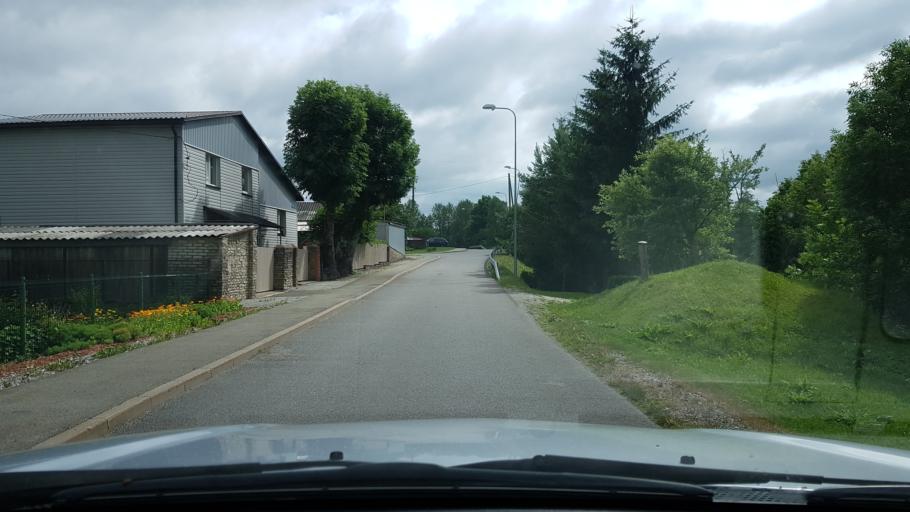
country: EE
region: Ida-Virumaa
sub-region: Narva linn
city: Narva
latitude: 59.3950
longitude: 28.1243
